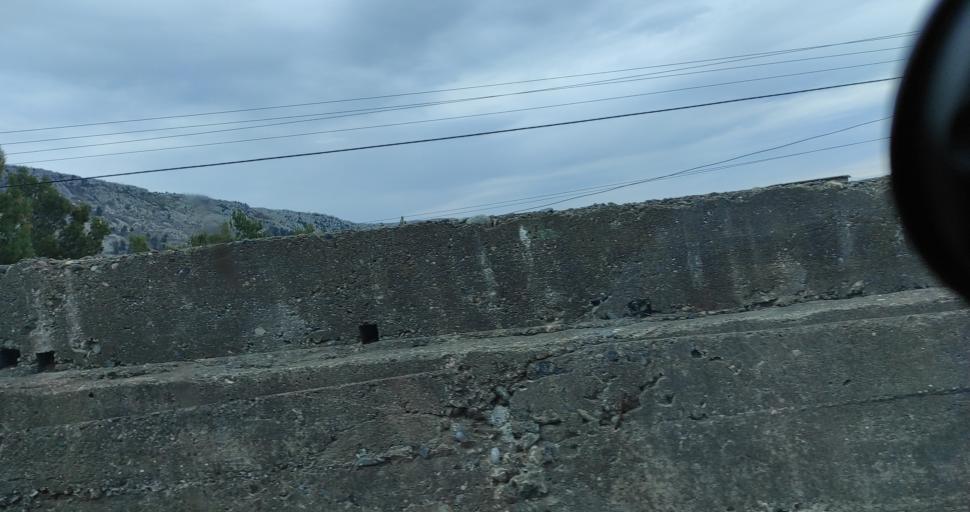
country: AL
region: Lezhe
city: Shengjin
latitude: 41.8115
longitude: 19.5846
